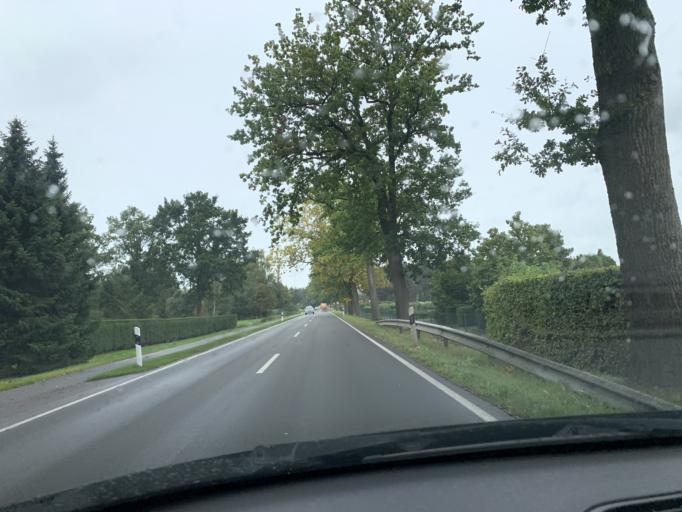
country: DE
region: Lower Saxony
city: Bad Zwischenahn
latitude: 53.1648
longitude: 8.0711
